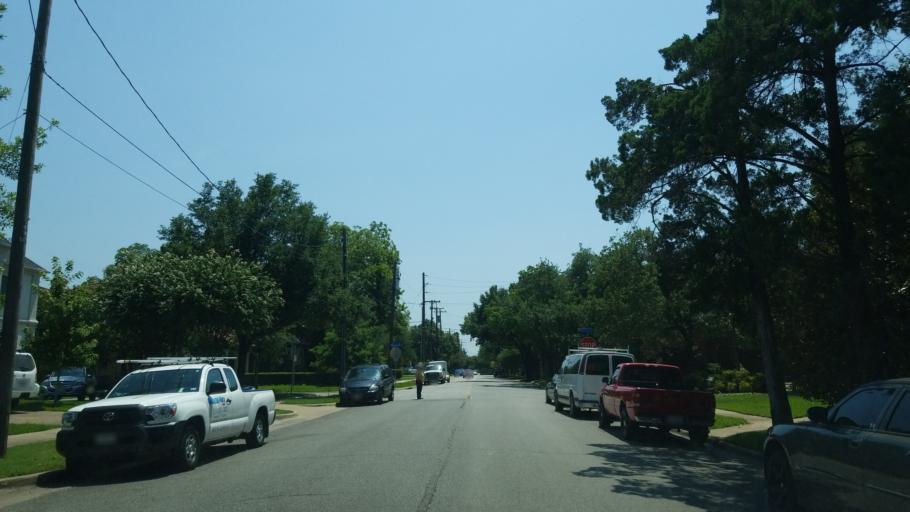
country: US
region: Texas
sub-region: Dallas County
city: Highland Park
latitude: 32.8293
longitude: -96.7866
